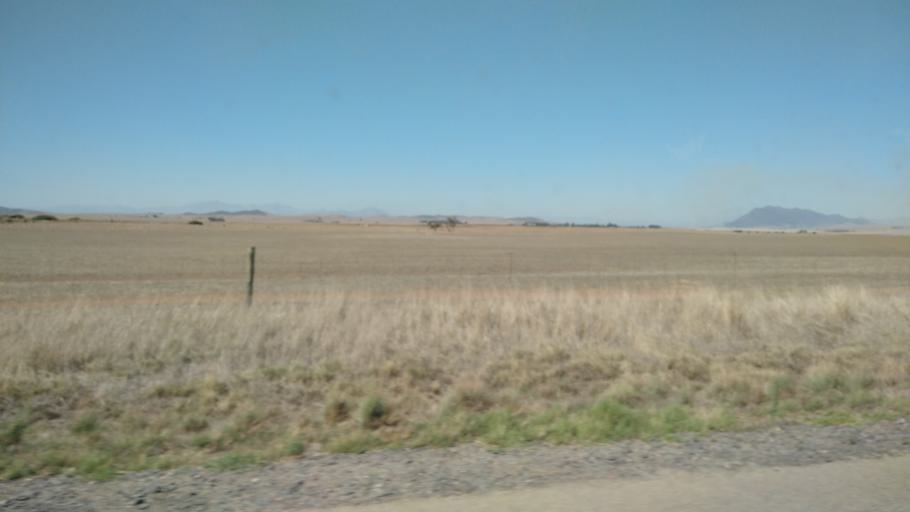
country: ZA
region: Western Cape
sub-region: West Coast District Municipality
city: Moorreesburg
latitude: -33.2759
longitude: 18.6017
